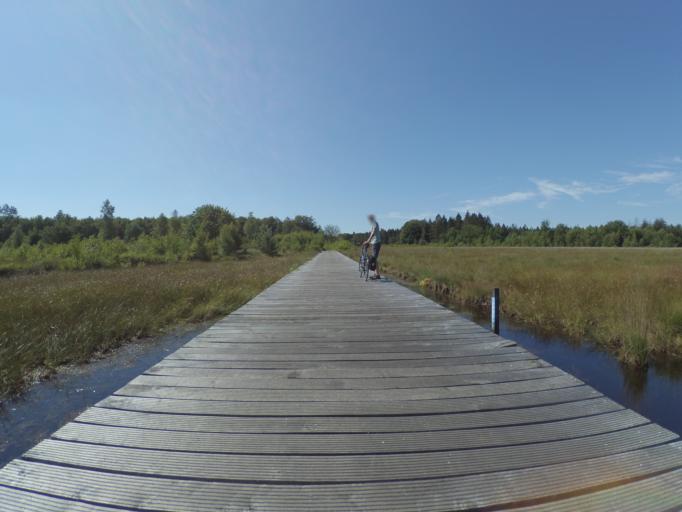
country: NL
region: Drenthe
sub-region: Gemeente Assen
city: Assen
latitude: 52.9154
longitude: 6.6556
